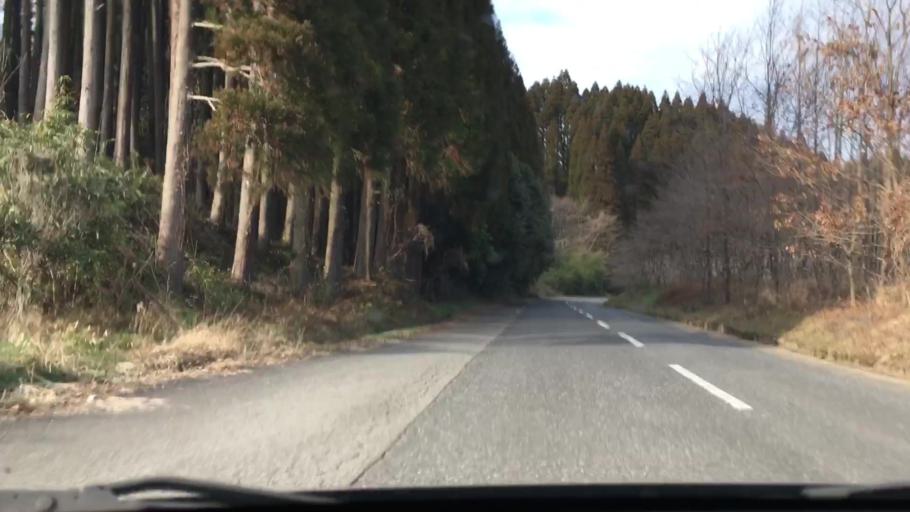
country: JP
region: Miyazaki
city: Nichinan
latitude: 31.6202
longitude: 131.3364
